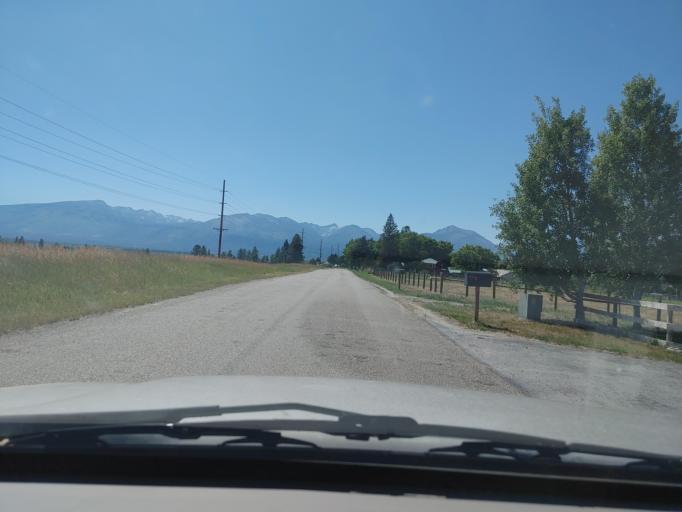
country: US
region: Montana
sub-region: Ravalli County
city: Hamilton
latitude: 46.2772
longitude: -114.0427
